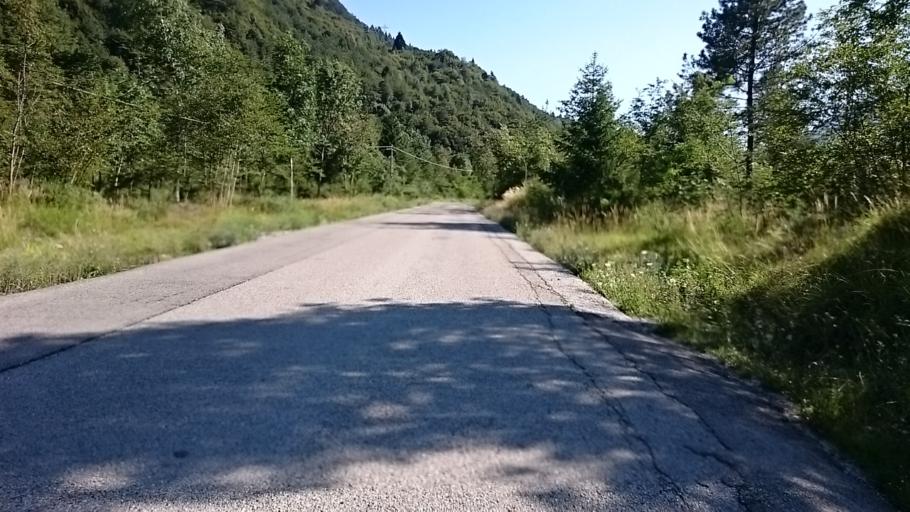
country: IT
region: Veneto
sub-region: Provincia di Belluno
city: Longarone
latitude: 46.2378
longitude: 12.3073
